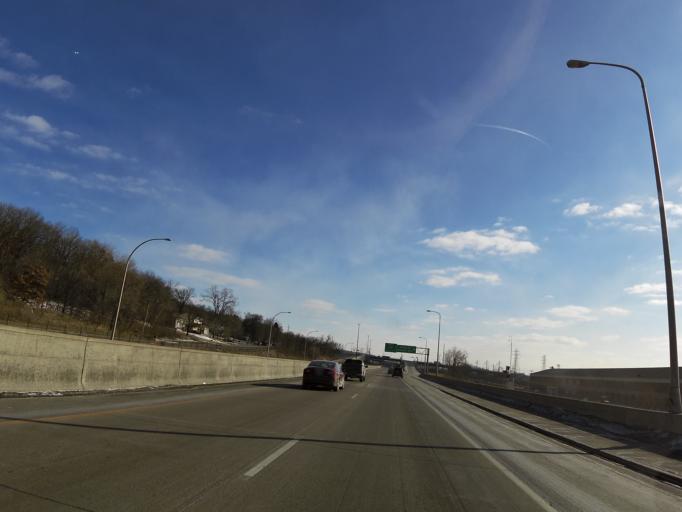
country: US
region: Minnesota
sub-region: Dakota County
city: South Saint Paul
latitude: 44.8972
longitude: -93.0093
